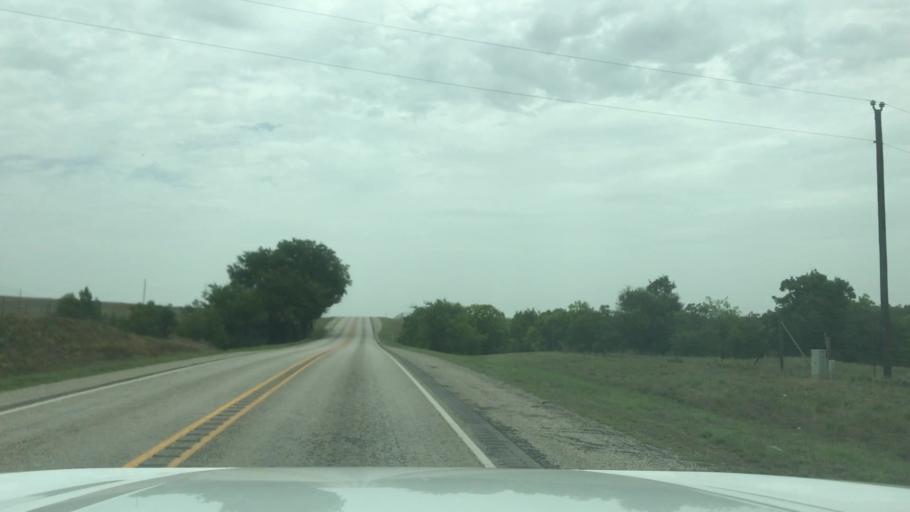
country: US
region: Texas
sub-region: Hamilton County
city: Hico
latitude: 32.0545
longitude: -98.1767
